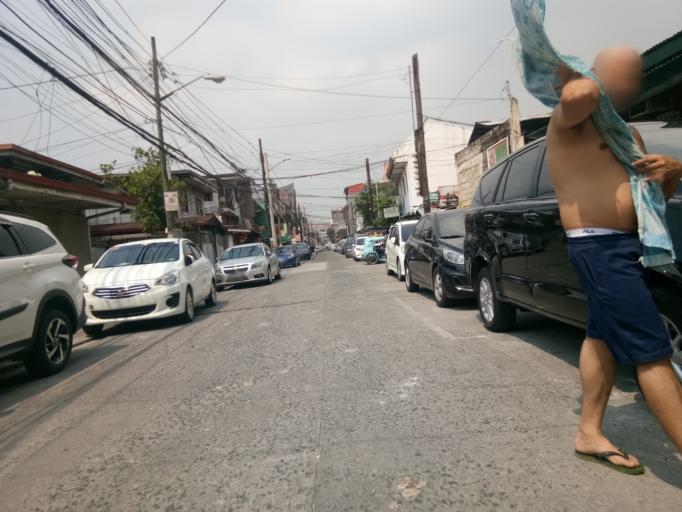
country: PH
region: Metro Manila
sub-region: Pasig
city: Pasig City
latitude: 14.6135
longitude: 121.0618
